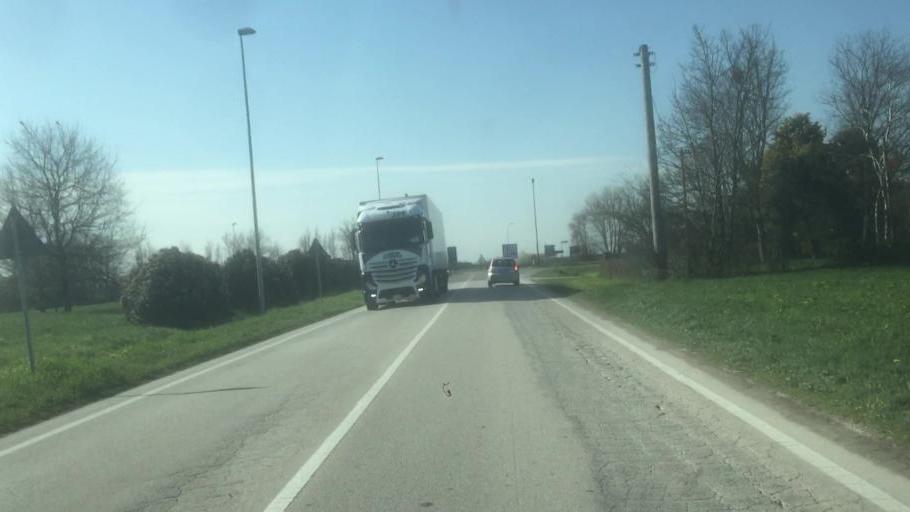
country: IT
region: Veneto
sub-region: Provincia di Rovigo
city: San Bellino
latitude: 45.0293
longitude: 11.5769
